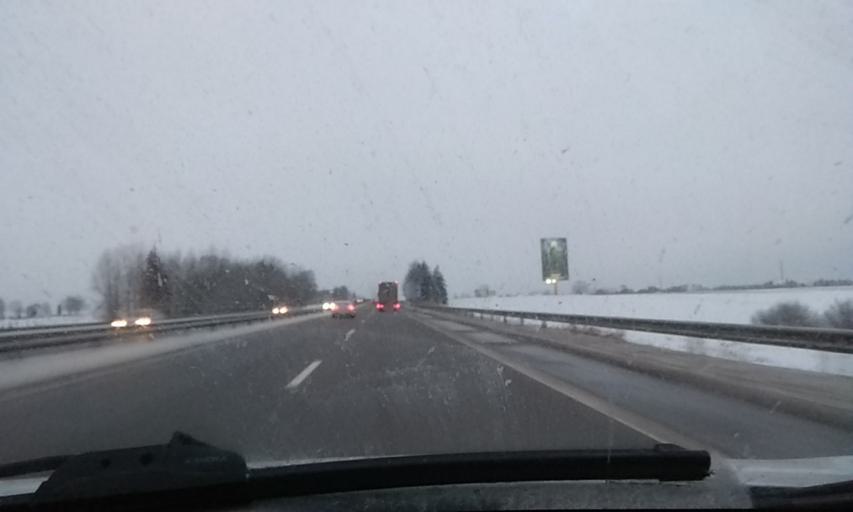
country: LT
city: Kaisiadorys
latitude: 54.8388
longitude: 24.3530
